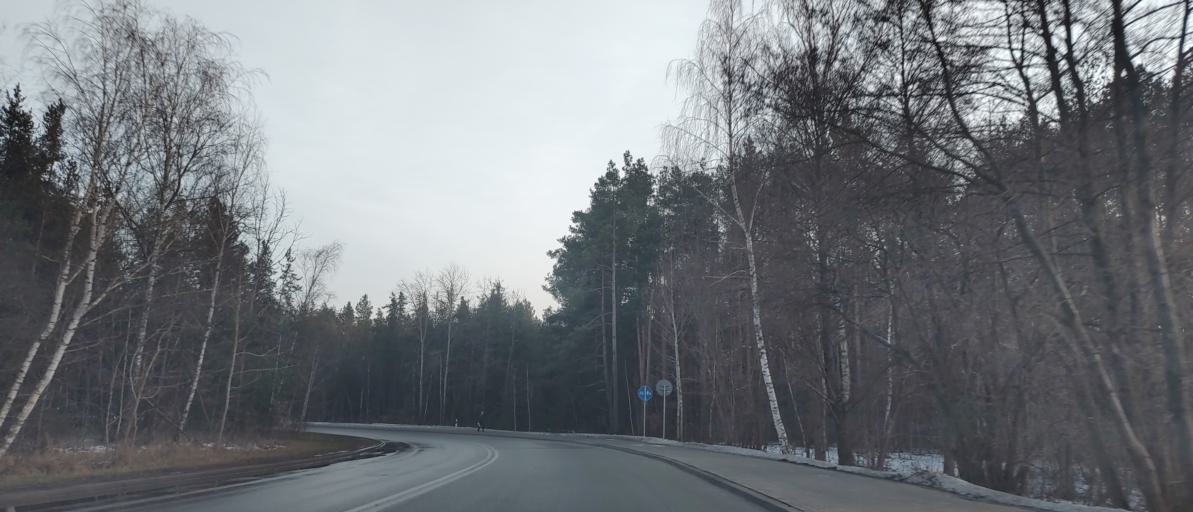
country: PL
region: Masovian Voivodeship
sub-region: Powiat bialobrzeski
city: Bialobrzegi
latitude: 51.6445
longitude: 20.9329
